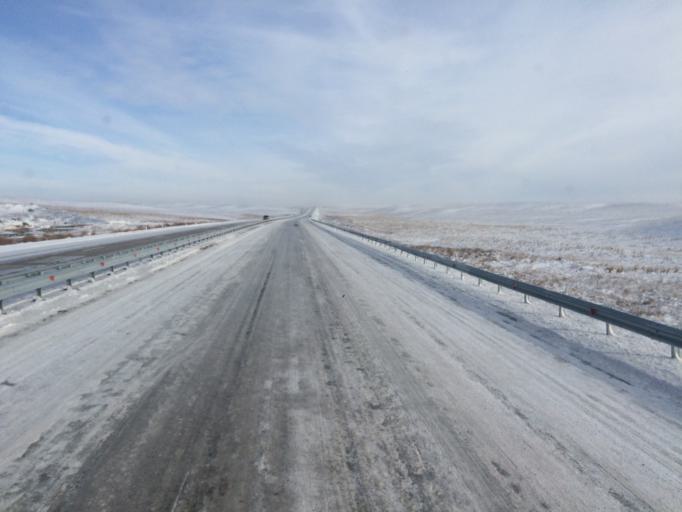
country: KZ
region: Zhambyl
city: Georgiyevka
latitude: 43.3550
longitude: 74.5711
